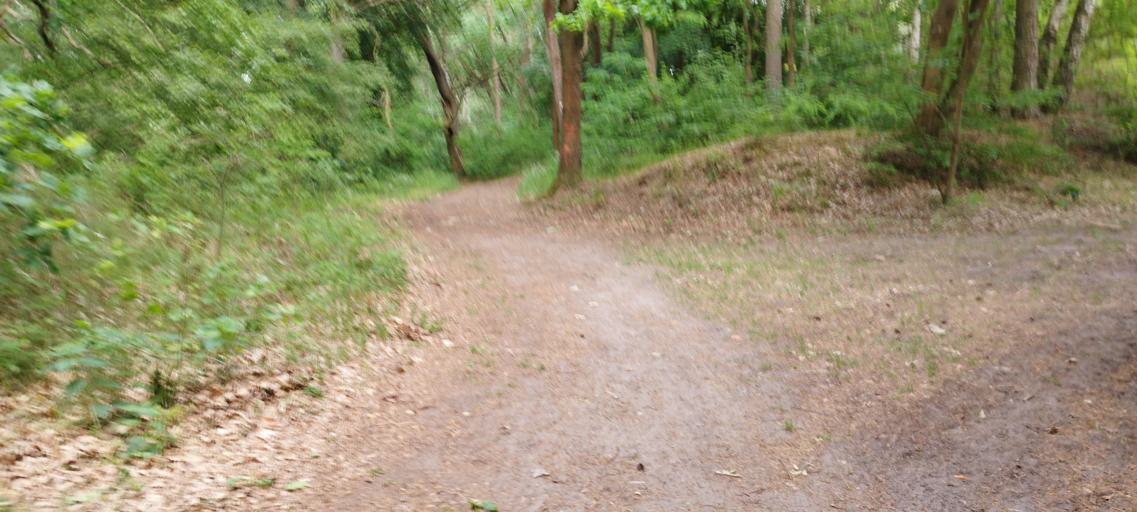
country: DE
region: Brandenburg
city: Furstenwalde
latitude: 52.3628
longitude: 14.0382
